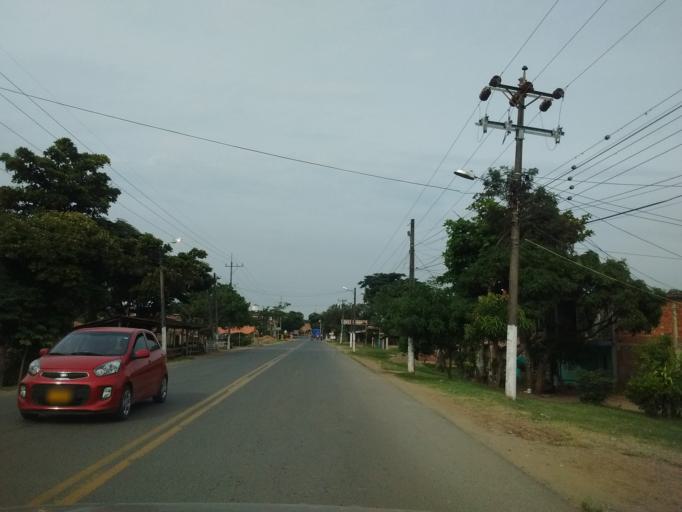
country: CO
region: Cauca
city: Puerto Tejada
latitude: 3.1762
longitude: -76.4565
